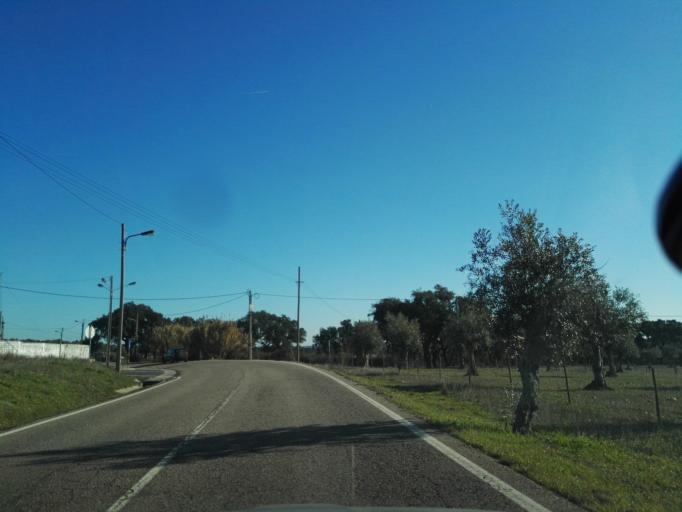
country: PT
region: Santarem
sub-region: Constancia
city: Constancia
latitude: 39.4820
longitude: -8.3028
